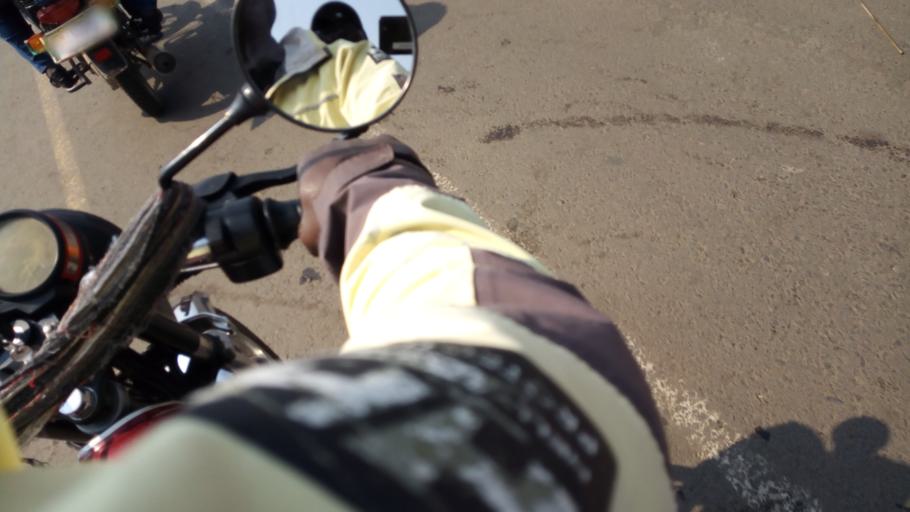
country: UG
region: Western Region
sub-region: Kisoro District
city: Kisoro
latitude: -1.3392
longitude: 29.7393
